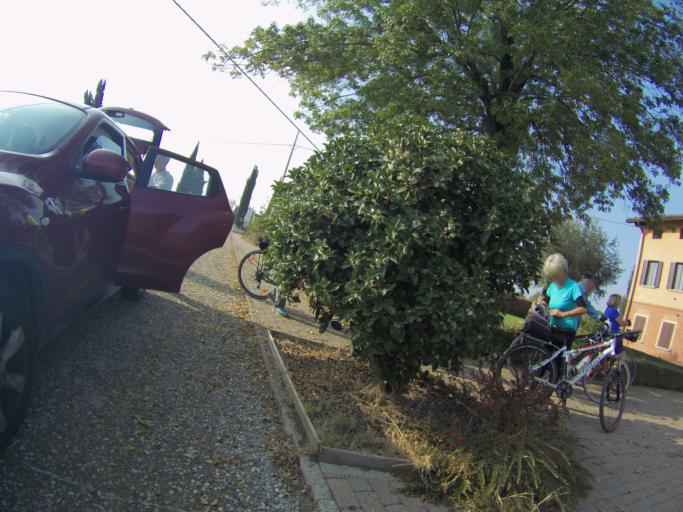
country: IT
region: Emilia-Romagna
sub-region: Provincia di Reggio Emilia
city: Montecavolo
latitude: 44.6514
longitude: 10.5323
